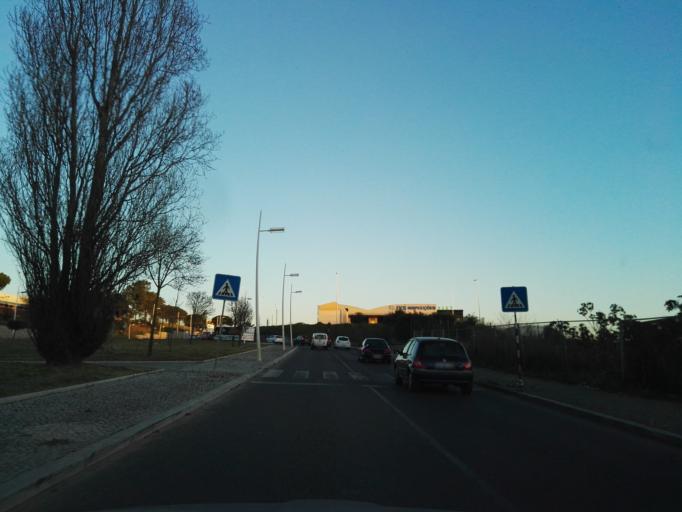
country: PT
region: Setubal
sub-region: Seixal
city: Corroios
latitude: 38.6334
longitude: -9.1425
